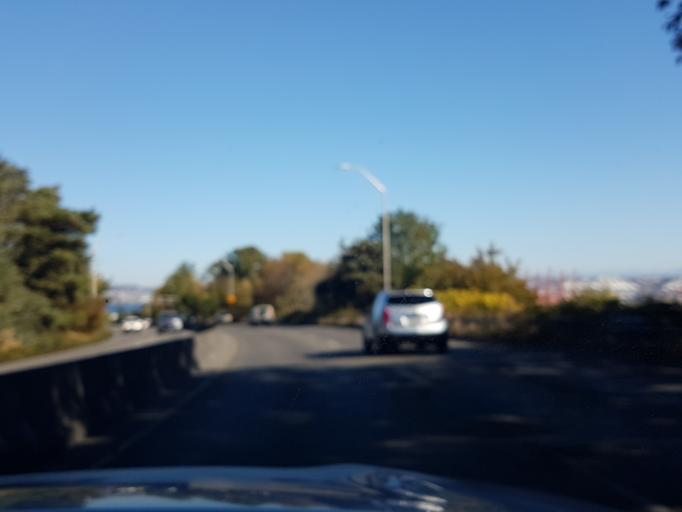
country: US
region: Washington
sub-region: King County
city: White Center
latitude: 47.5664
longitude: -122.3739
